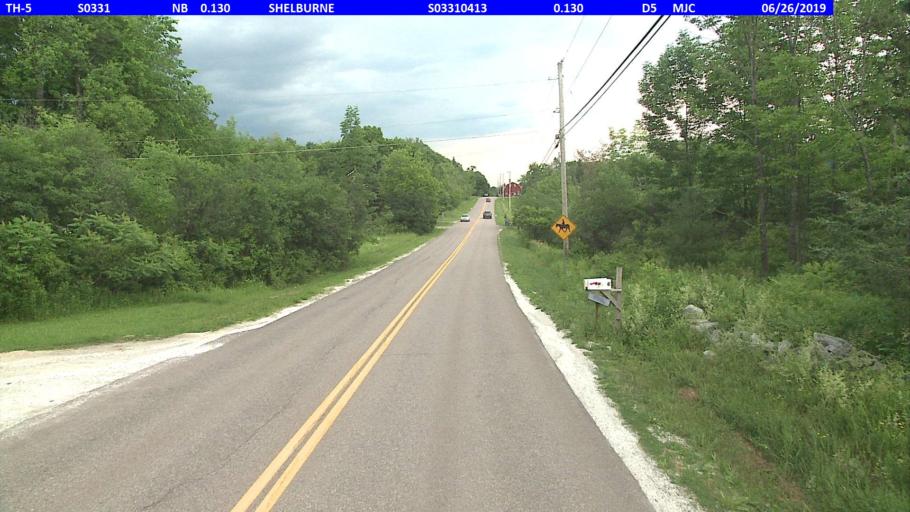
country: US
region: Vermont
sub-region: Chittenden County
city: Hinesburg
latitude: 44.3734
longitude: -73.1809
